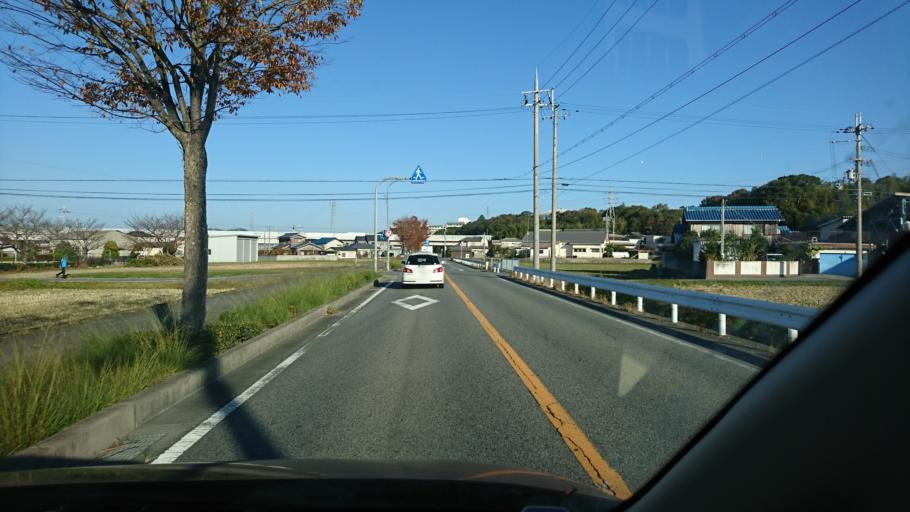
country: JP
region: Hyogo
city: Kakogawacho-honmachi
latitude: 34.7667
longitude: 134.8855
